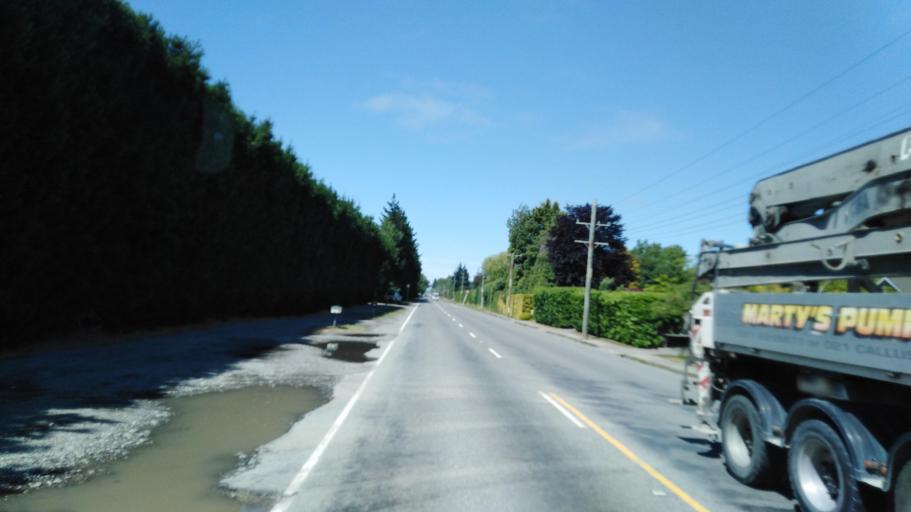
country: NZ
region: Canterbury
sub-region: Selwyn District
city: Prebbleton
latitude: -43.5143
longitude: 172.5079
